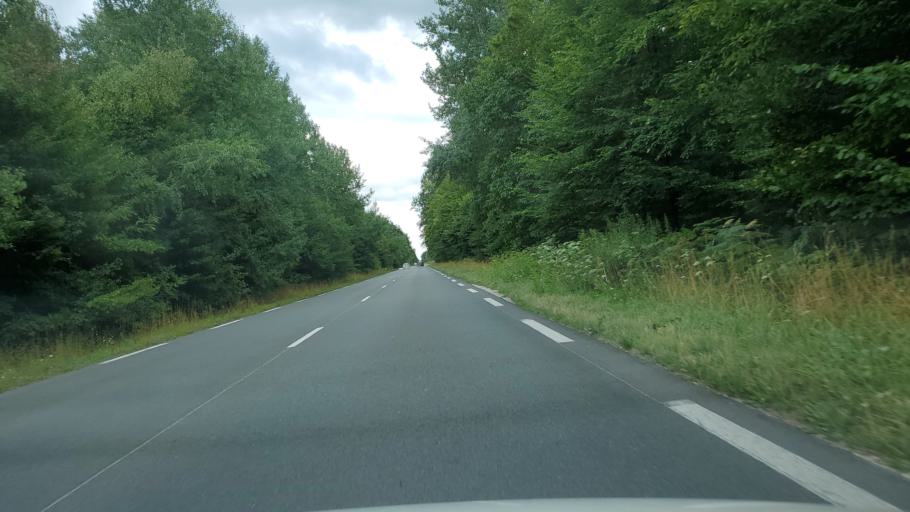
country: FR
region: Ile-de-France
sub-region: Departement de Seine-et-Marne
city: Mortcerf
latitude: 48.7649
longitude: 2.9204
